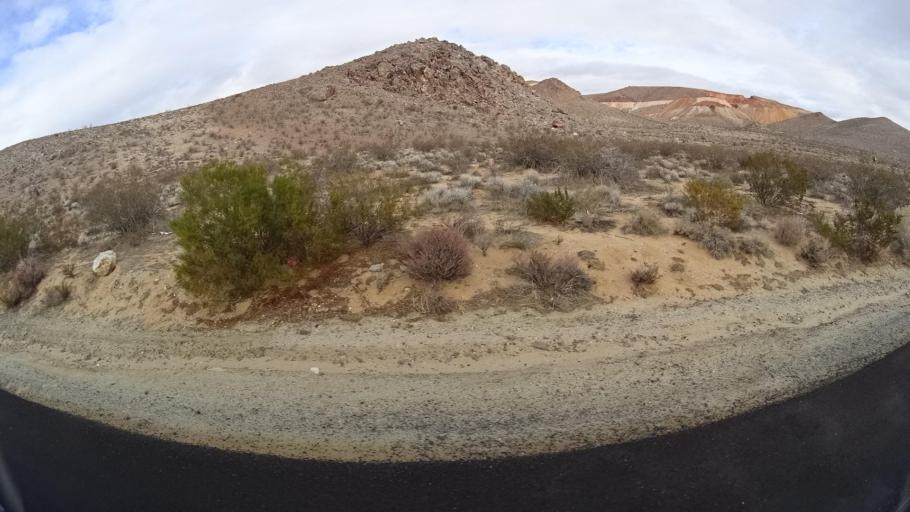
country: US
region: California
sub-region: Kern County
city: Rosamond
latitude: 34.9494
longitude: -118.2849
